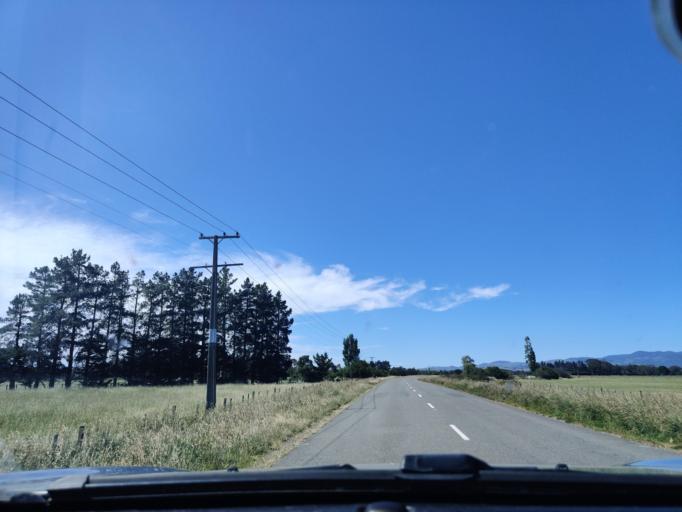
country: NZ
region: Wellington
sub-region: South Wairarapa District
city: Waipawa
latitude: -41.1671
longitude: 175.3668
